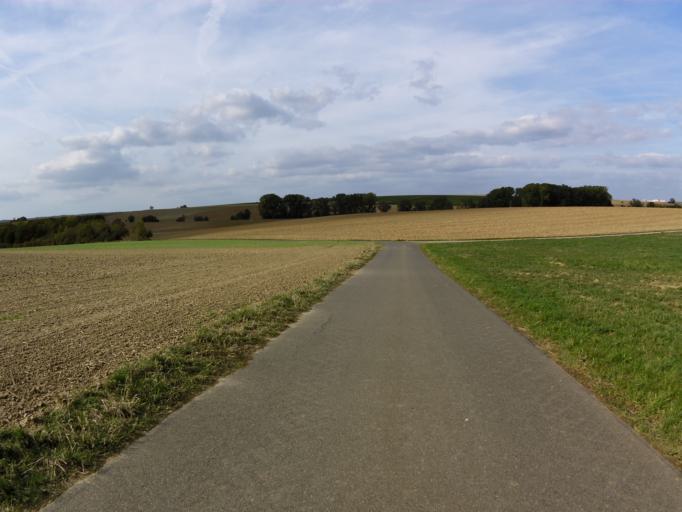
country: DE
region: Bavaria
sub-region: Regierungsbezirk Unterfranken
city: Eibelstadt
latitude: 49.7030
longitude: 9.9552
